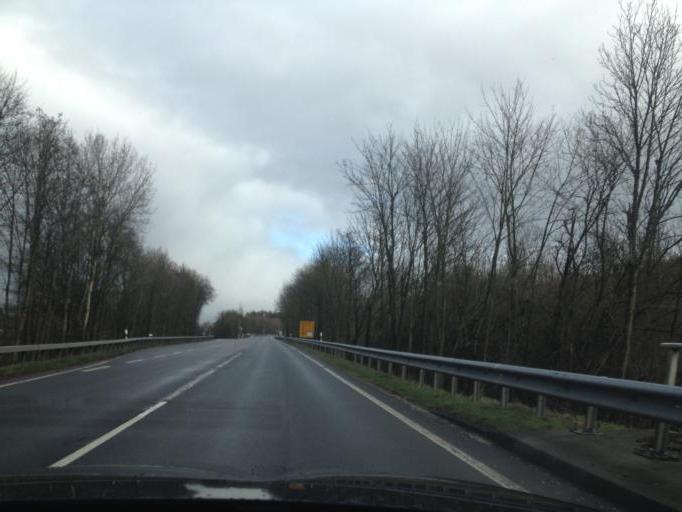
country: DE
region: Rheinland-Pfalz
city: Birkenfeld
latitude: 49.6472
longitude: 7.1719
